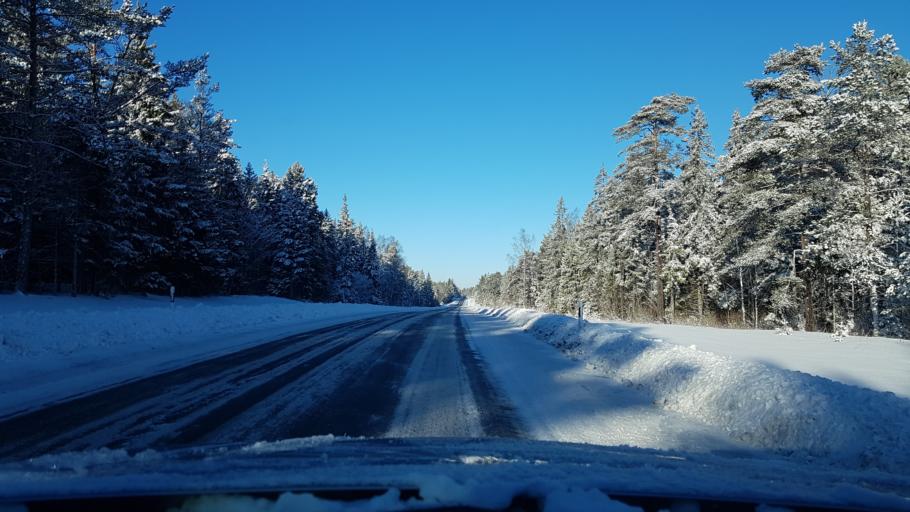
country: EE
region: Hiiumaa
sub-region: Kaerdla linn
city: Kardla
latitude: 58.9661
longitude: 22.8340
